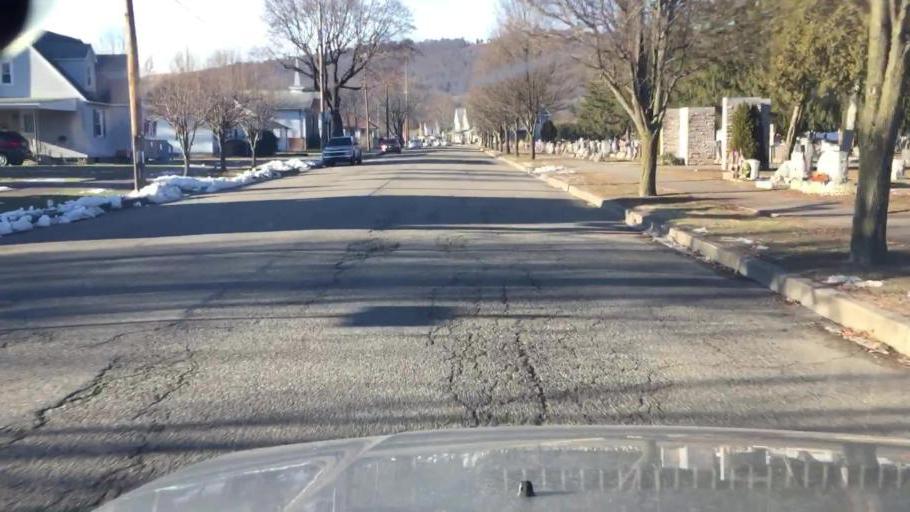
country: US
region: Pennsylvania
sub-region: Columbia County
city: Berwick
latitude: 41.0667
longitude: -76.2364
